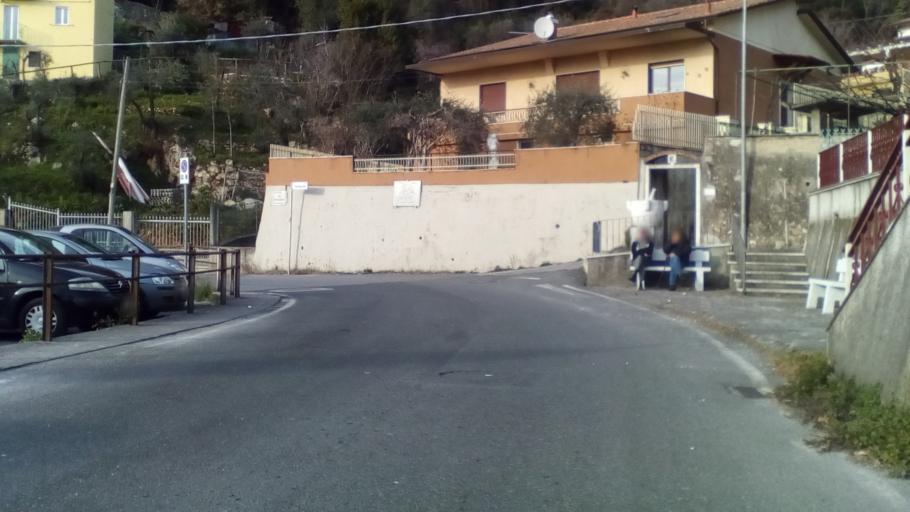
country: IT
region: Tuscany
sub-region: Provincia di Massa-Carrara
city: Carrara
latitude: 44.0834
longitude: 10.1137
